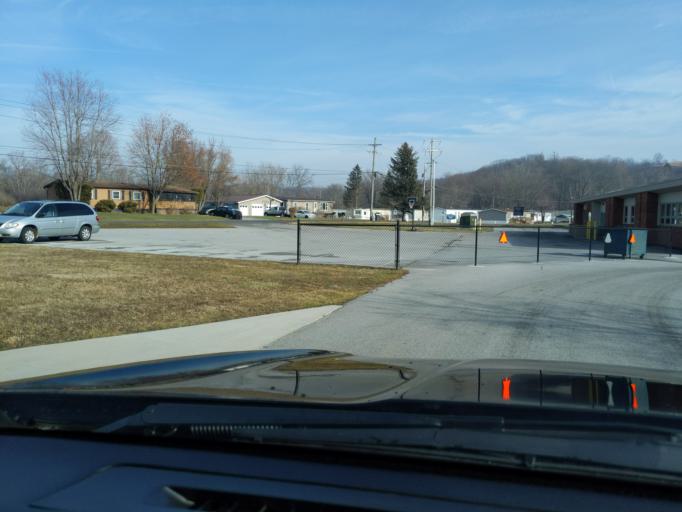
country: US
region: Pennsylvania
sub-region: Blair County
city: Duncansville
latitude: 40.4433
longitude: -78.4281
